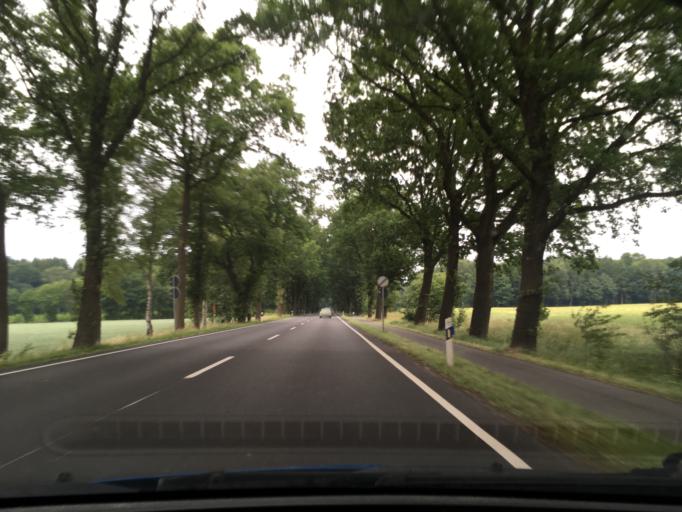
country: DE
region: Lower Saxony
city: Drestedt
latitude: 53.3360
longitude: 9.8120
